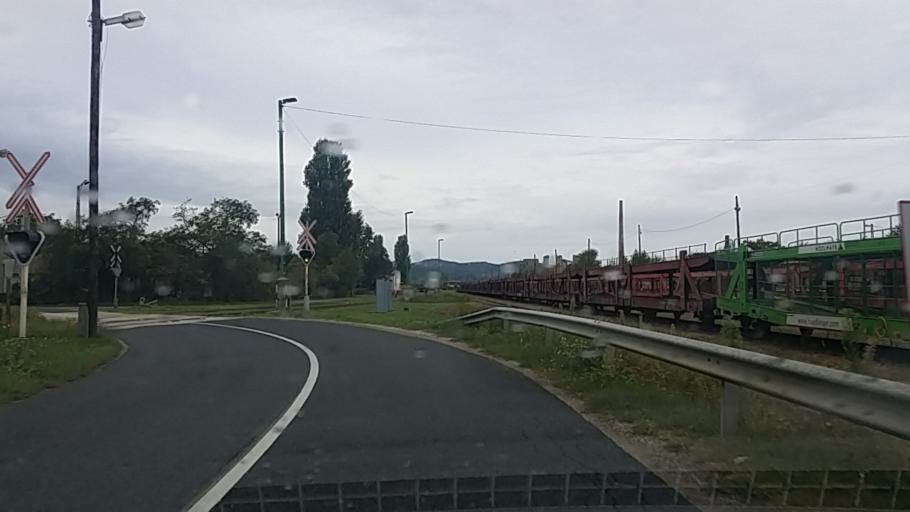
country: HU
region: Komarom-Esztergom
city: Tokod
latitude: 47.7346
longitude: 18.6756
